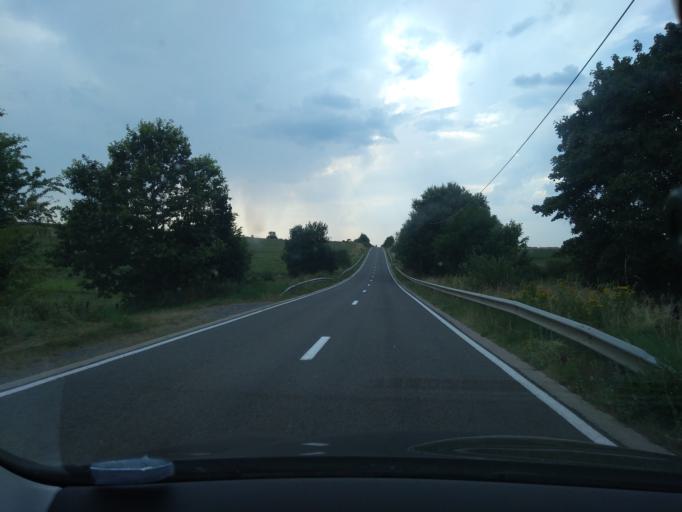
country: BE
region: Wallonia
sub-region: Province du Luxembourg
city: Bertogne
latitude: 50.0806
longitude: 5.6842
